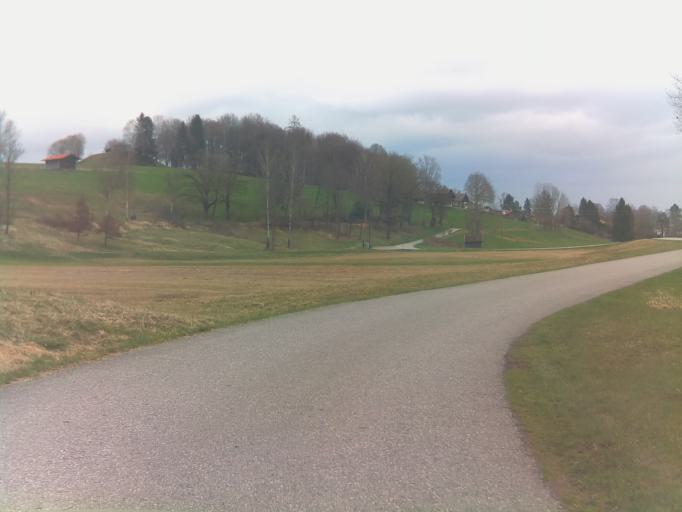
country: DE
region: Bavaria
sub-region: Upper Bavaria
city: Uffing
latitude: 47.7086
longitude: 11.1358
